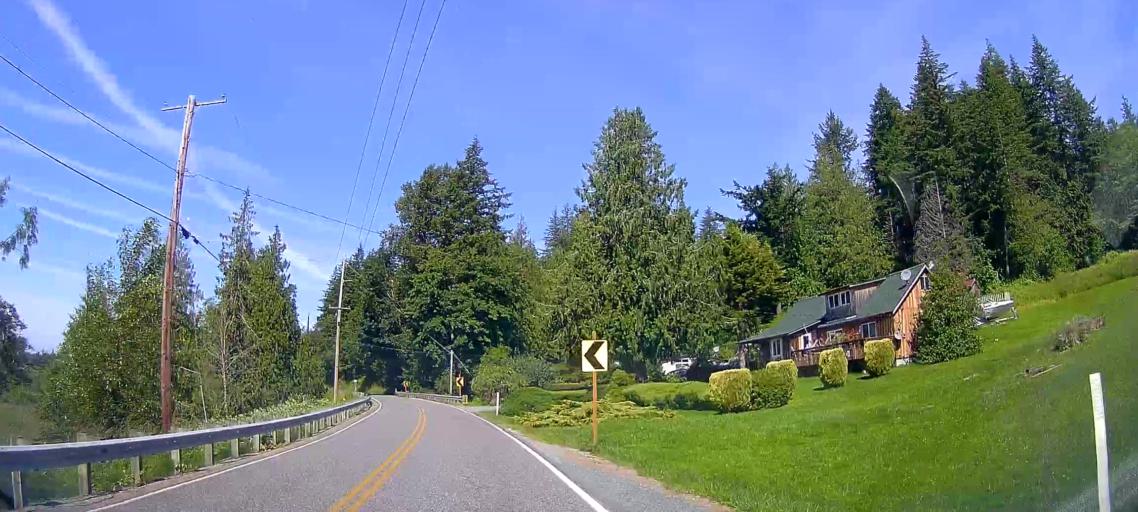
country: US
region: Washington
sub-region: Skagit County
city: Sedro-Woolley
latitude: 48.5345
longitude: -122.2896
